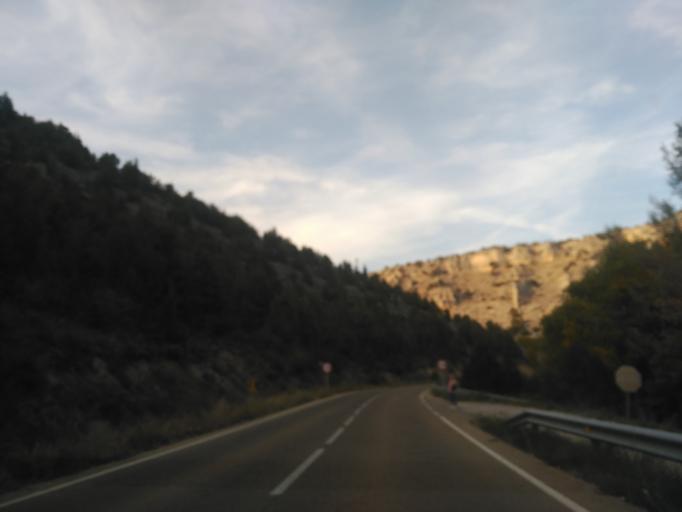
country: ES
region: Castille and Leon
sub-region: Provincia de Soria
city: Ucero
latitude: 41.7295
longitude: -3.0480
